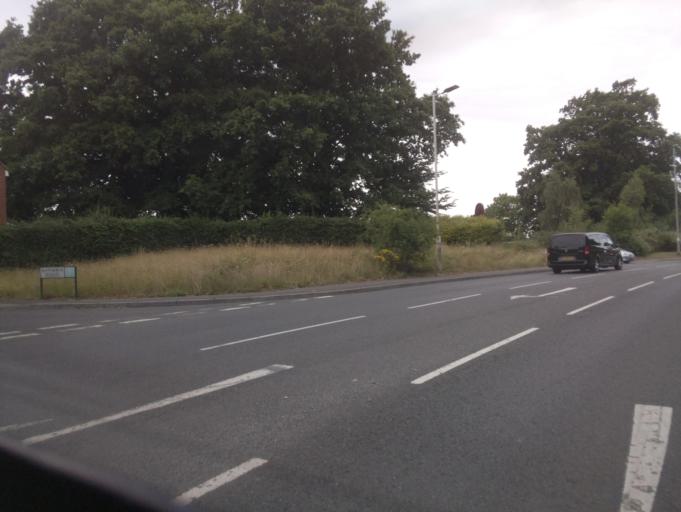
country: GB
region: England
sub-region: Devon
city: Heavitree
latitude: 50.7178
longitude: -3.4778
